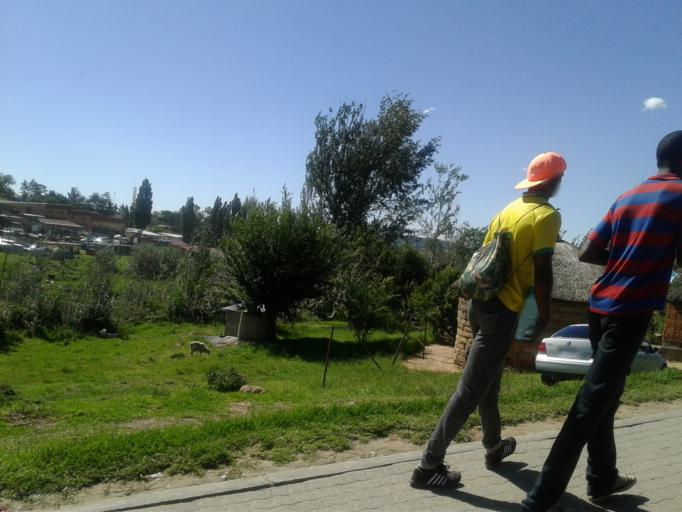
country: LS
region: Butha-Buthe
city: Butha-Buthe
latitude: -28.7665
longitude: 28.2539
